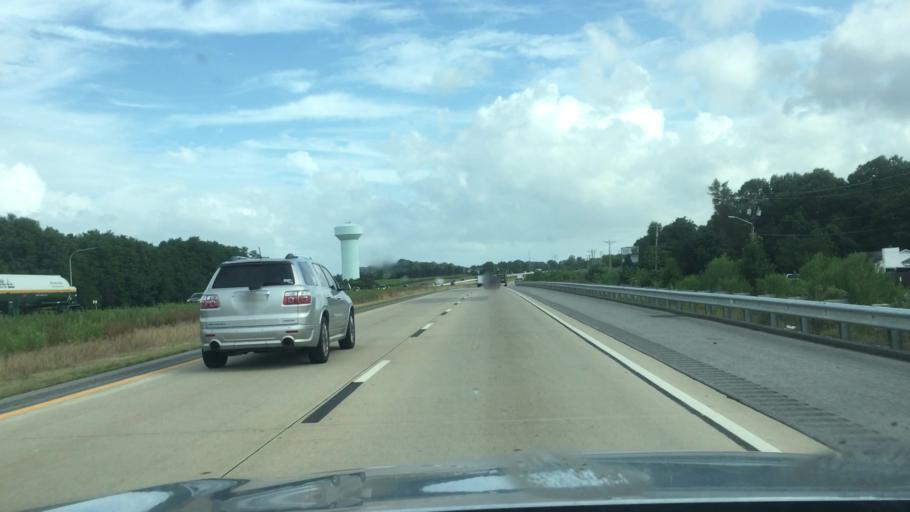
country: US
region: Delaware
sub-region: New Castle County
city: Townsend
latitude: 39.4297
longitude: -75.6594
